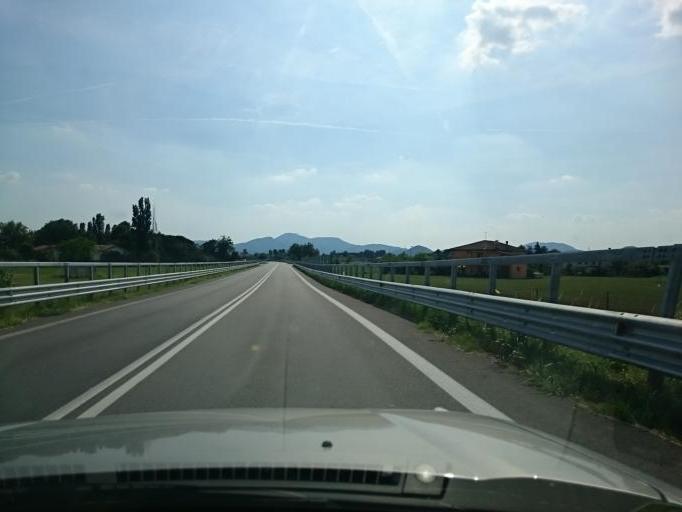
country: IT
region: Veneto
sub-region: Provincia di Padova
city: Abano Terme
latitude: 45.3654
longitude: 11.8144
